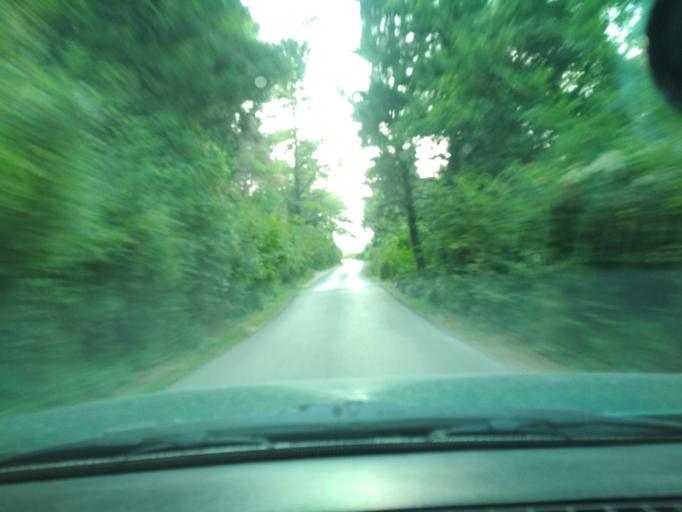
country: ME
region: Kotor
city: Kotor
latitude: 42.3981
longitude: 18.7658
